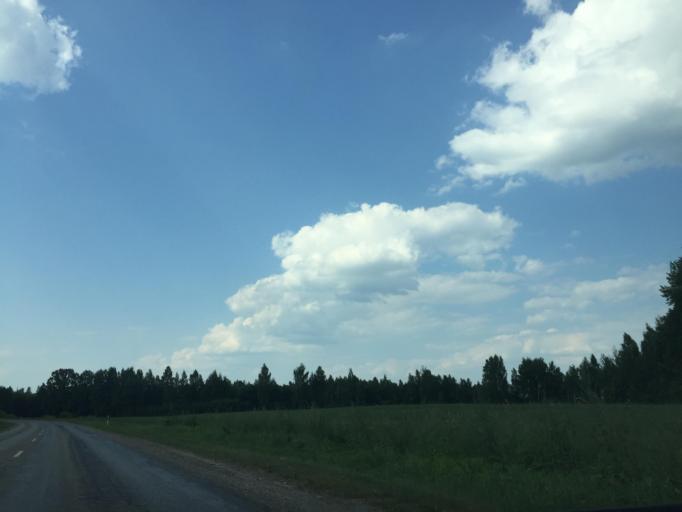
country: LV
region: Pargaujas
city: Stalbe
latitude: 57.3769
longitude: 25.0268
